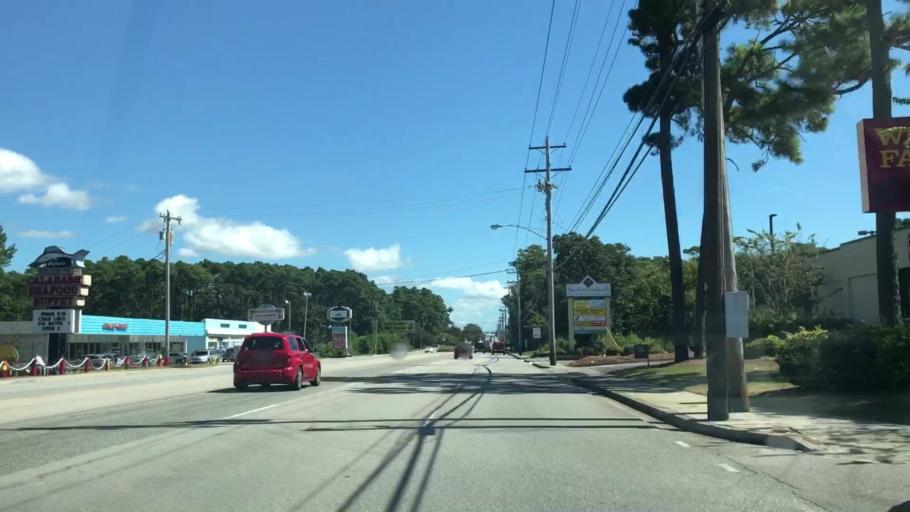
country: US
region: South Carolina
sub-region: Horry County
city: North Myrtle Beach
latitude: 33.8182
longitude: -78.6922
